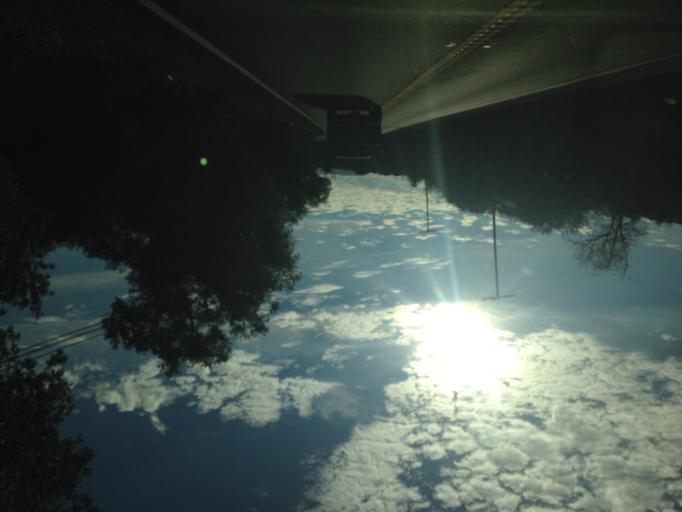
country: US
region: California
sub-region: San Diego County
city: Rainbow
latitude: 33.3531
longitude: -117.0269
